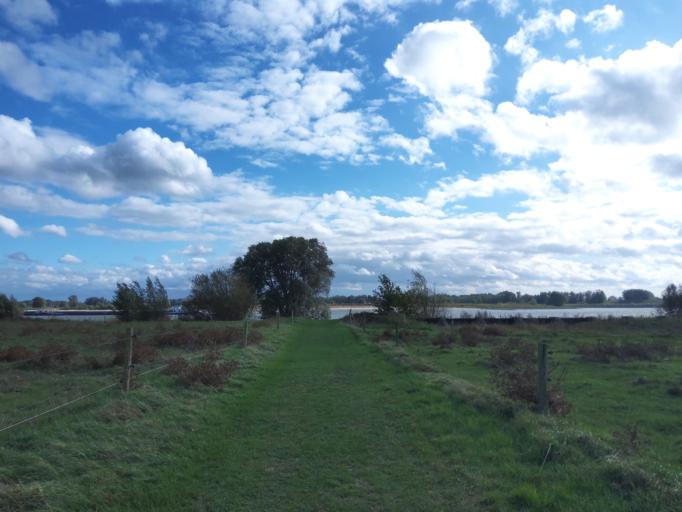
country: NL
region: Gelderland
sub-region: Gemeente Neerijnen
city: Neerijnen
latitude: 51.8249
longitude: 5.2841
